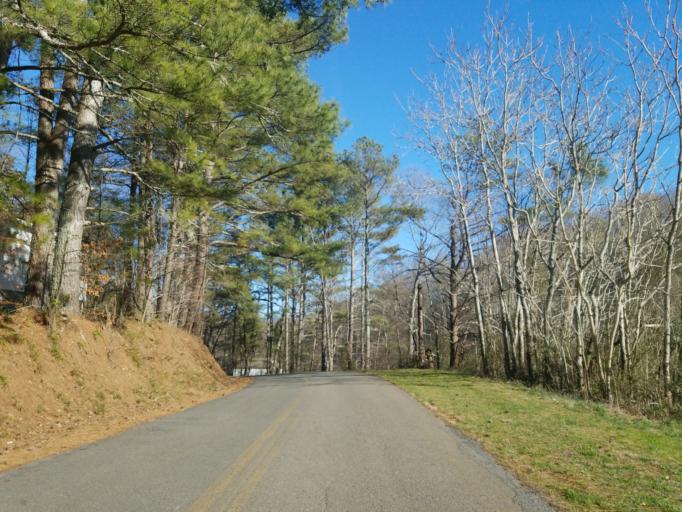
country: US
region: Georgia
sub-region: Gilmer County
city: Ellijay
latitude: 34.6443
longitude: -84.3477
